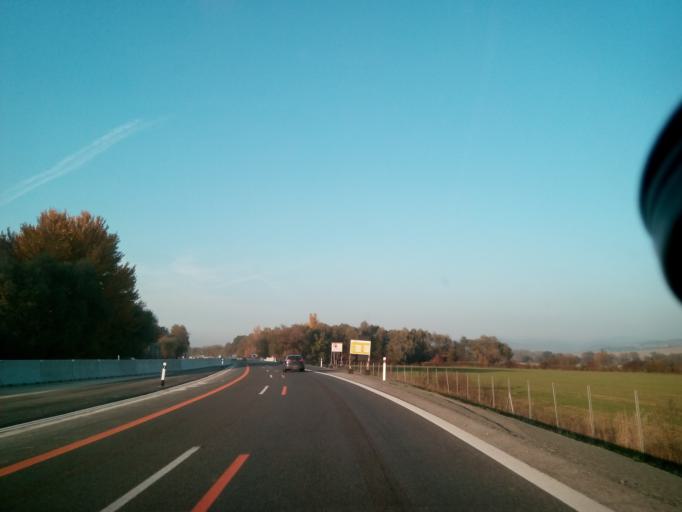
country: SK
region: Kosicky
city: Kosice
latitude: 48.7904
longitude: 21.3131
